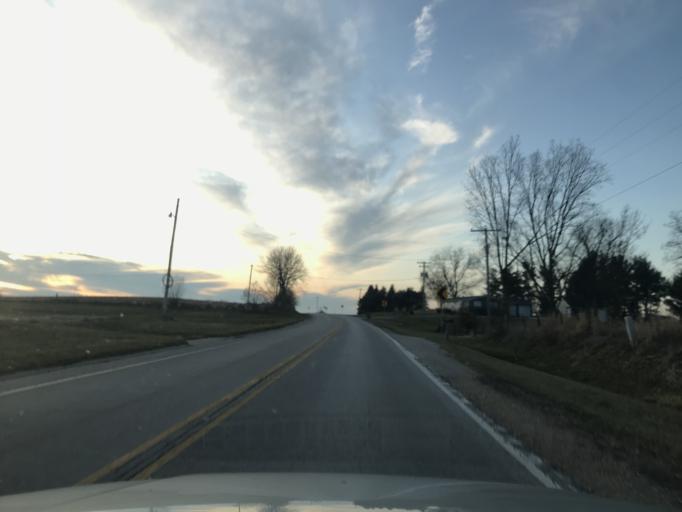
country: US
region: Illinois
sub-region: Warren County
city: Monmouth
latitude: 41.0251
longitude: -90.7739
